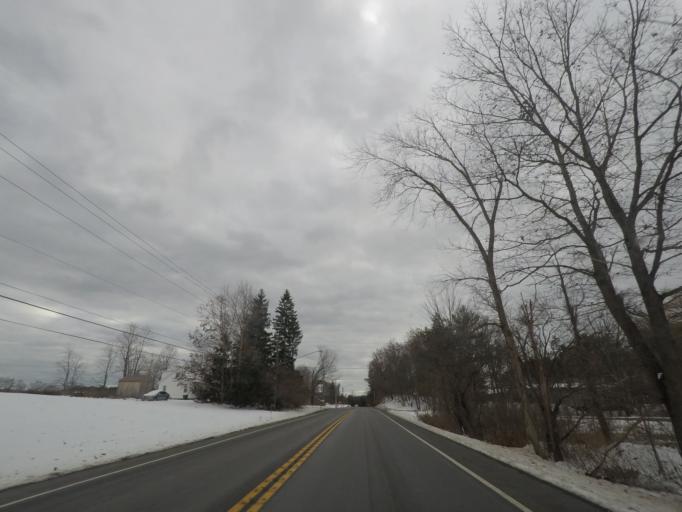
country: US
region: New York
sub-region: Rensselaer County
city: West Sand Lake
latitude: 42.6141
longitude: -73.6047
